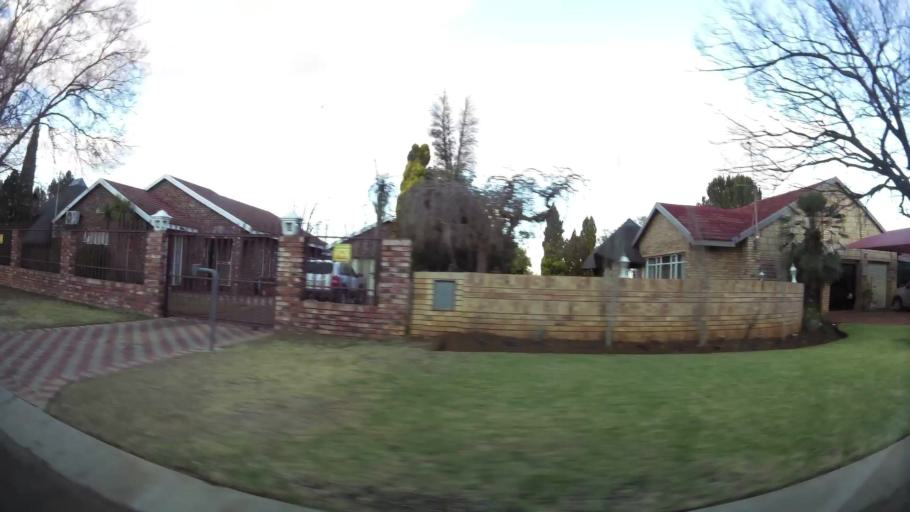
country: ZA
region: North-West
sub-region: Dr Kenneth Kaunda District Municipality
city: Potchefstroom
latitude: -26.7425
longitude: 27.1000
